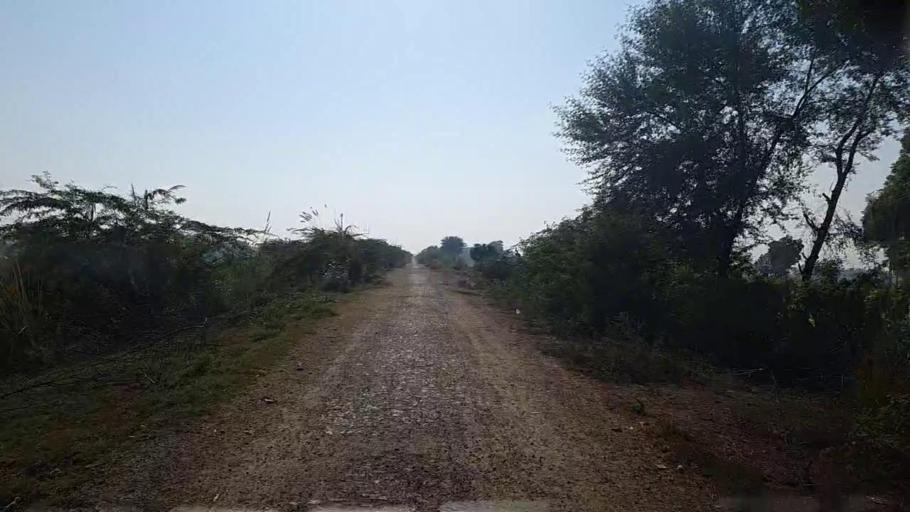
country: PK
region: Sindh
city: Pad Idan
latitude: 26.7823
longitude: 68.3354
